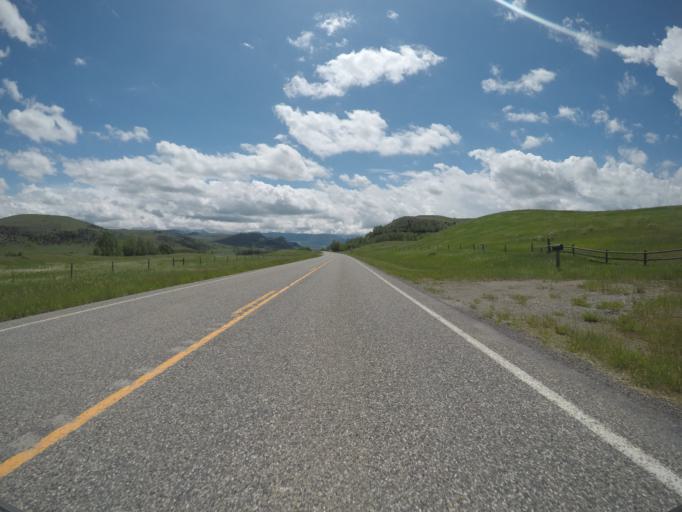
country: US
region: Montana
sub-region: Sweet Grass County
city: Big Timber
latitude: 45.6596
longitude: -110.1138
